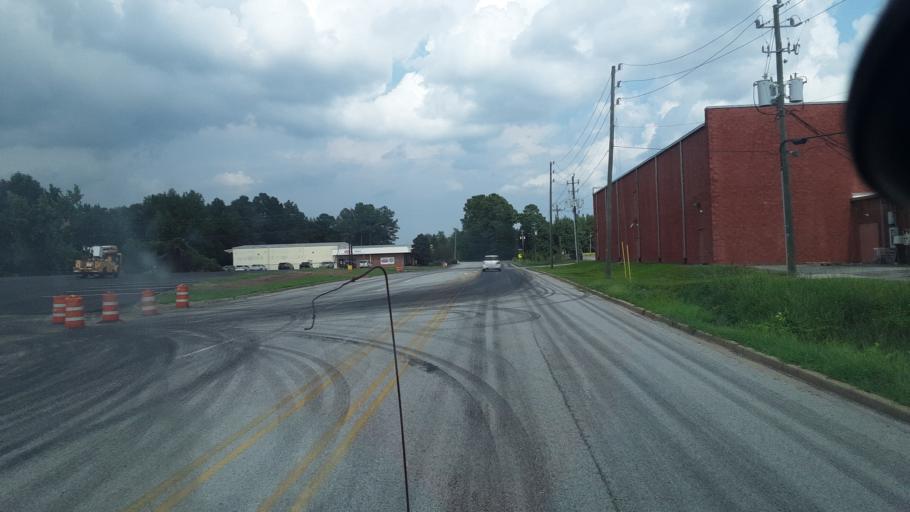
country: US
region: South Carolina
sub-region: Sumter County
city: Sumter
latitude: 33.9545
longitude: -80.3779
